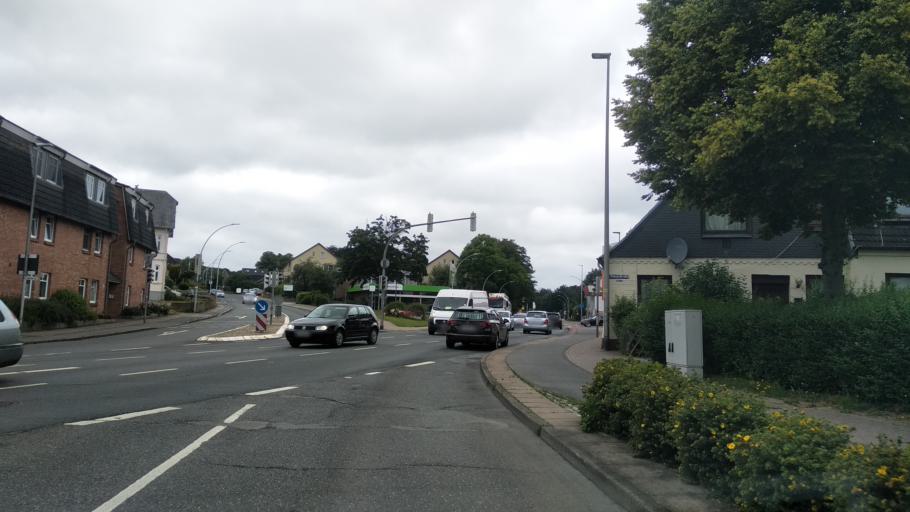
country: DE
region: Schleswig-Holstein
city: Schleswig
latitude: 54.5235
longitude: 9.5437
